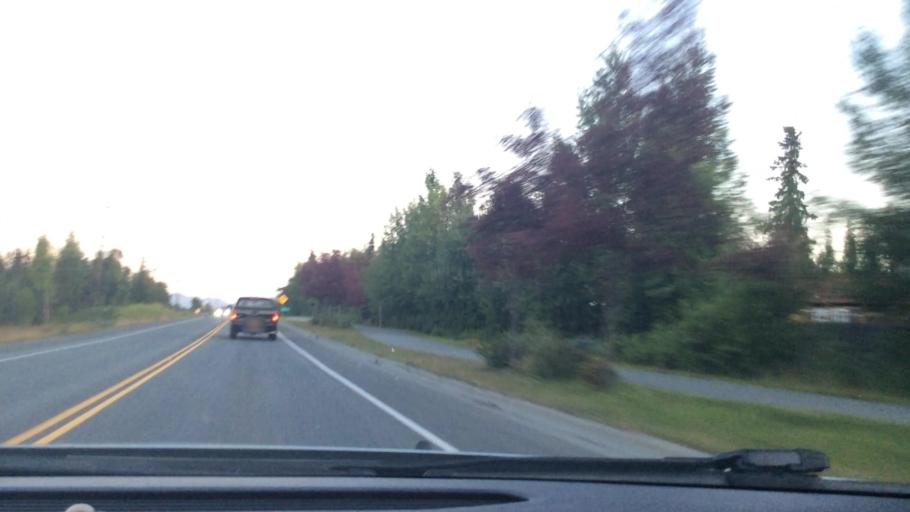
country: US
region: Alaska
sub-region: Anchorage Municipality
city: Anchorage
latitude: 61.1552
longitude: -149.8042
